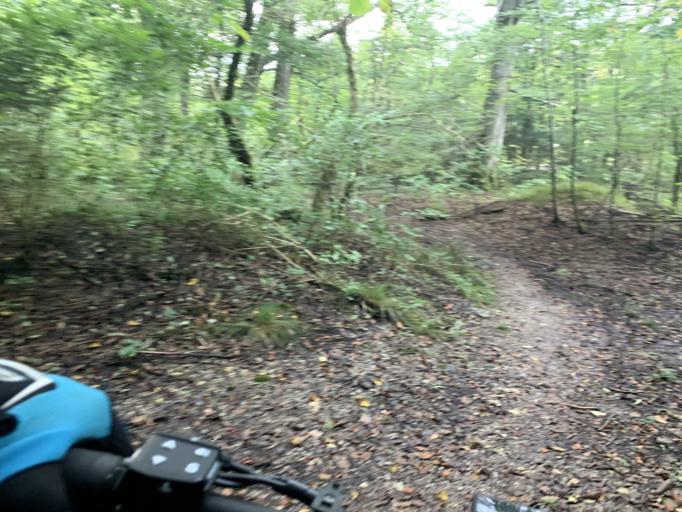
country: DE
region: Bavaria
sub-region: Upper Bavaria
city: Grunwald
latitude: 48.0383
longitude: 11.5141
